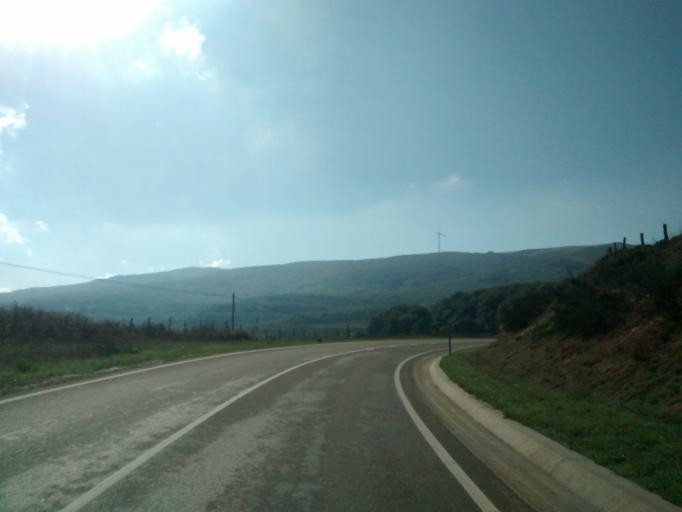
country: ES
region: Cantabria
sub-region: Provincia de Cantabria
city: Reinosa
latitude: 42.9825
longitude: -4.1043
